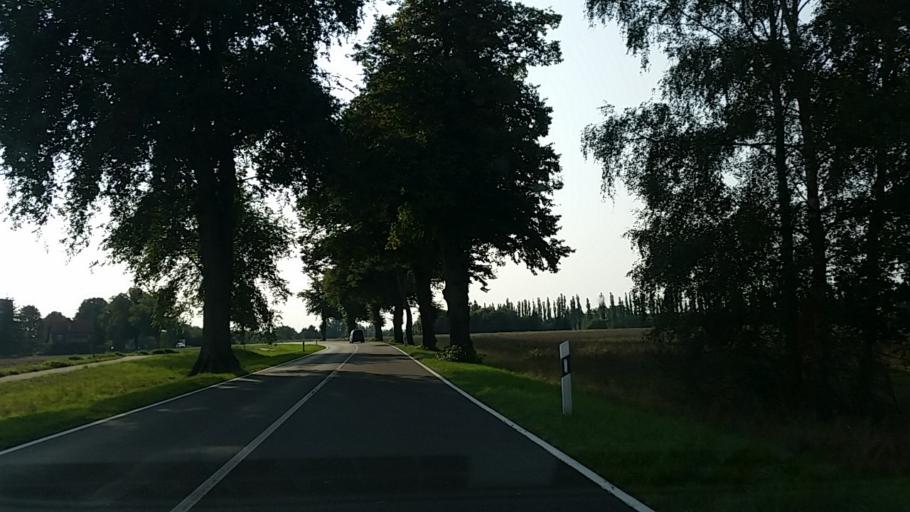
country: DE
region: Mecklenburg-Vorpommern
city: Hagenow
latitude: 53.4452
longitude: 11.1766
